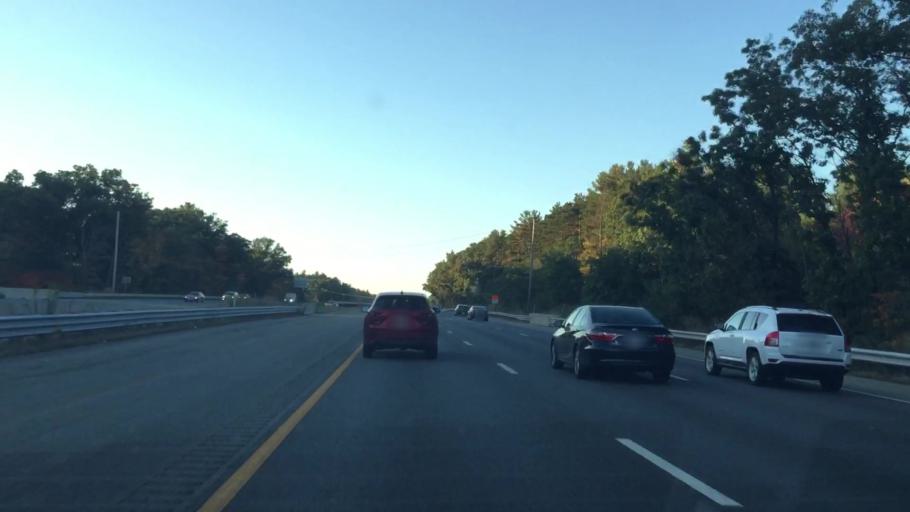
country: US
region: Massachusetts
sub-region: Middlesex County
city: Billerica
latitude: 42.5537
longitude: -71.2919
